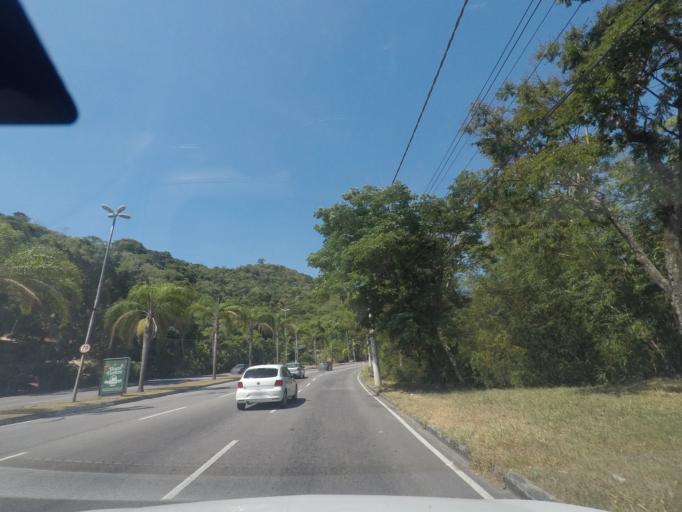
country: BR
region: Rio de Janeiro
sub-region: Niteroi
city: Niteroi
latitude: -22.9248
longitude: -43.0605
